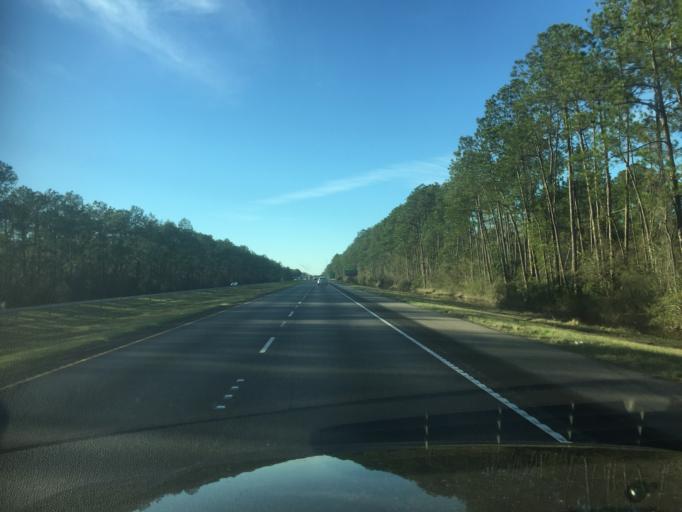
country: US
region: Louisiana
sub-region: Saint Tammany Parish
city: Lacombe
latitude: 30.3470
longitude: -89.9100
